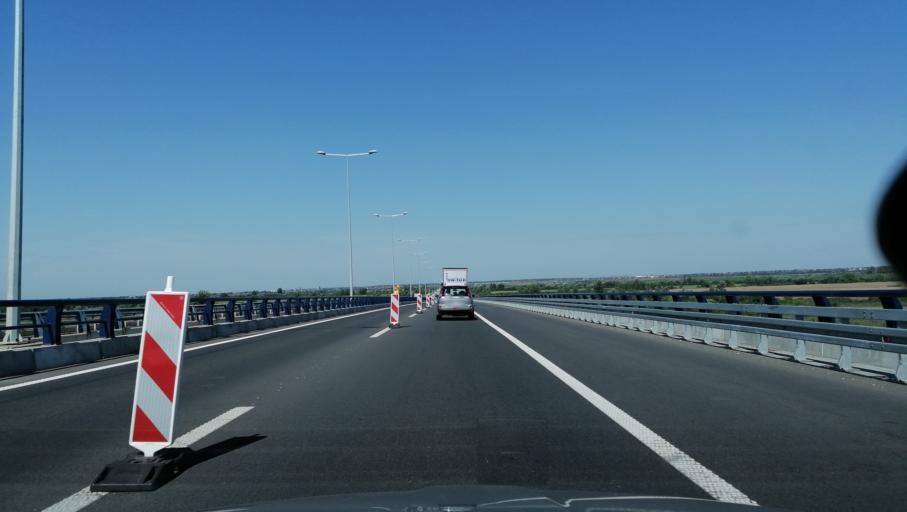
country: RS
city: Ostruznica
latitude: 44.7444
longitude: 20.3155
